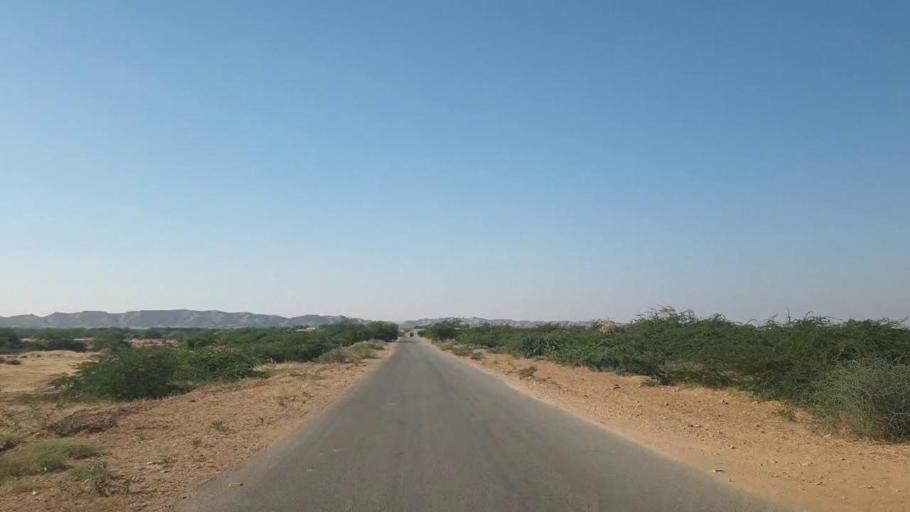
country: PK
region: Sindh
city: Malir Cantonment
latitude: 25.2828
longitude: 67.5809
